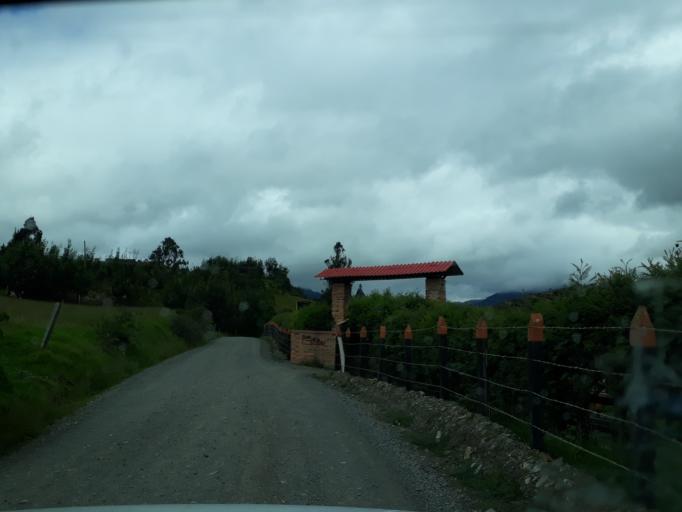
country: CO
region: Cundinamarca
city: Carmen de Carupa
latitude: 5.3203
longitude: -73.8893
